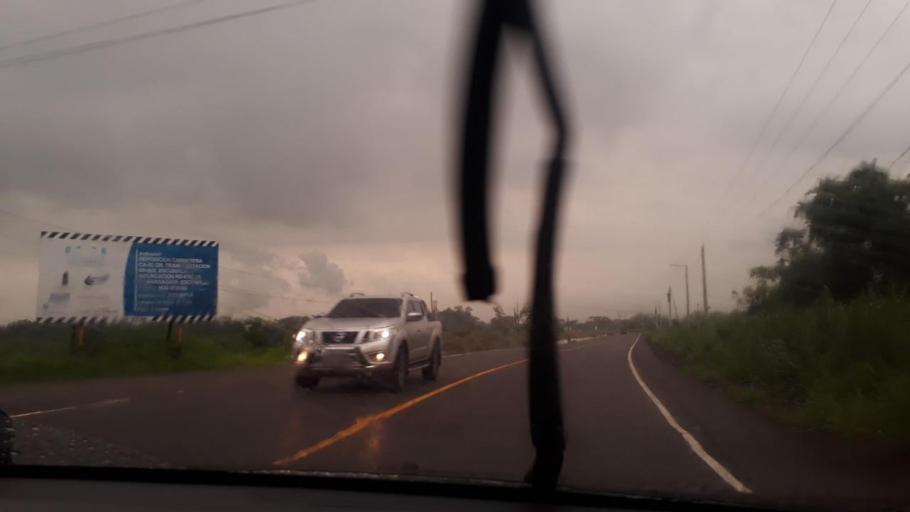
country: GT
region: Escuintla
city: Guanagazapa
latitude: 14.1017
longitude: -90.6165
